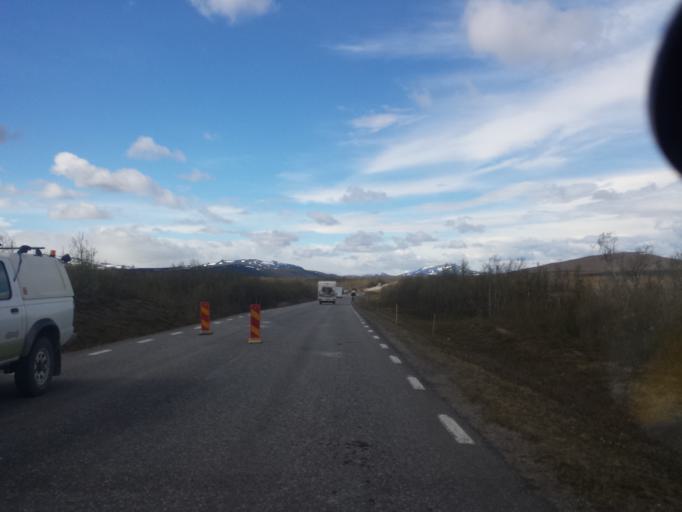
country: SE
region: Norrbotten
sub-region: Kiruna Kommun
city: Kiruna
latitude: 68.0106
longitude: 19.8444
